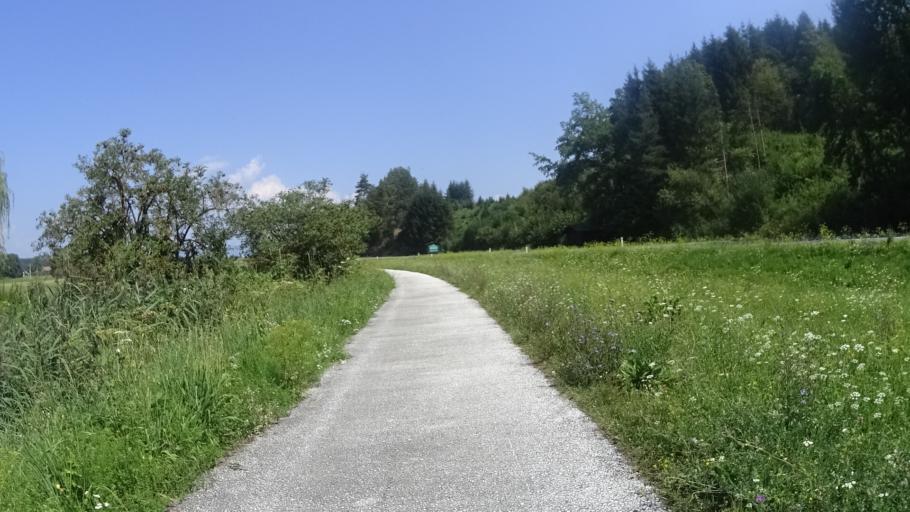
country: AT
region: Carinthia
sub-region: Politischer Bezirk Volkermarkt
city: Eberndorf
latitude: 46.5682
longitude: 14.6312
